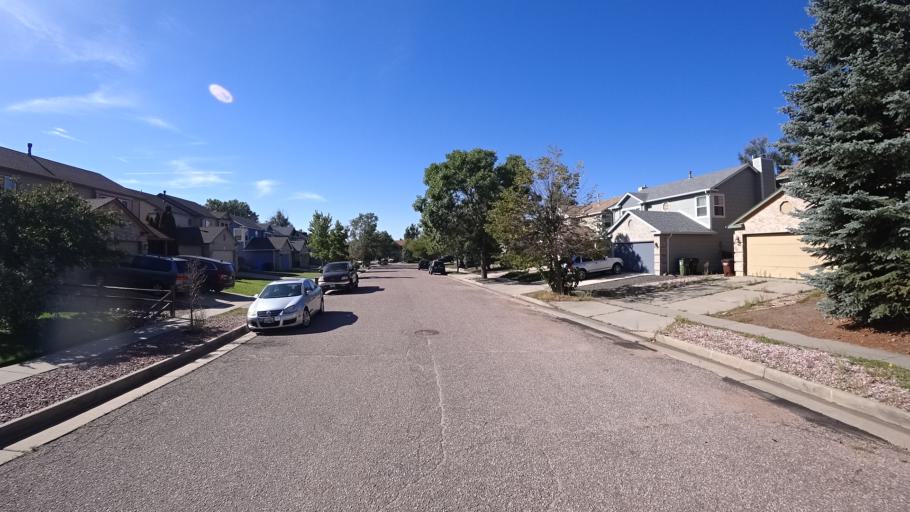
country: US
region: Colorado
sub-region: El Paso County
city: Black Forest
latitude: 38.9486
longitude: -104.7329
